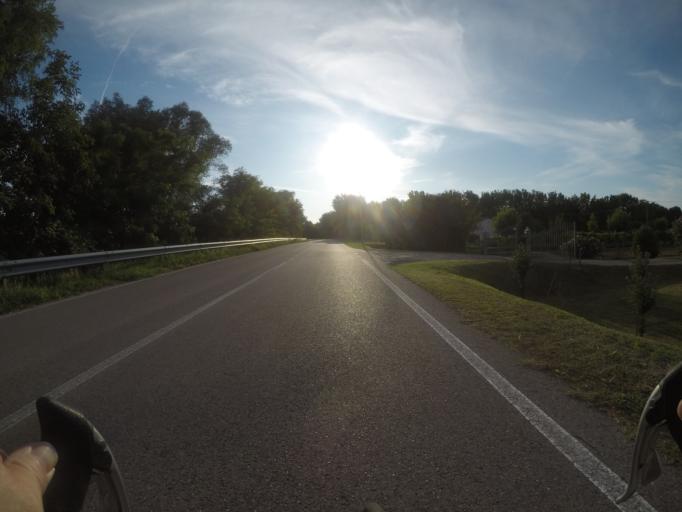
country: IT
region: Veneto
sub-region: Provincia di Rovigo
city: Pincara
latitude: 45.0036
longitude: 11.6276
